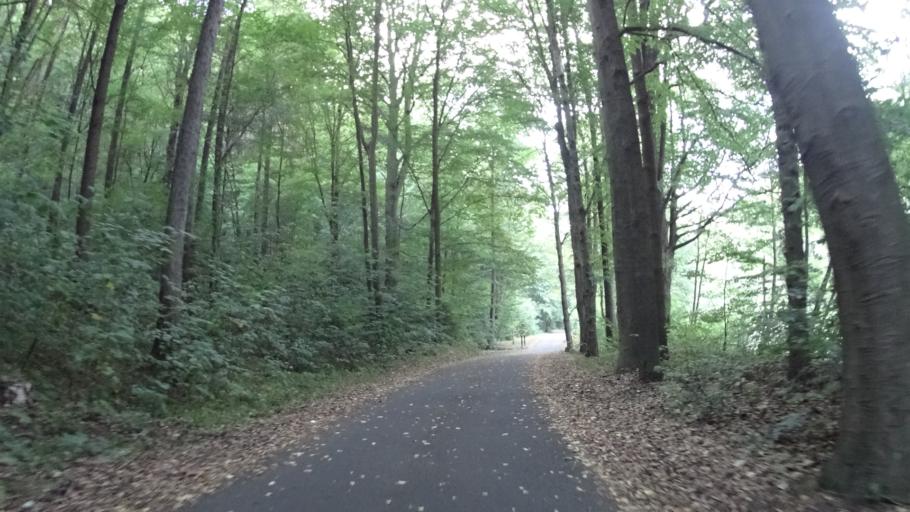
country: DE
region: Saxony
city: Ostritz
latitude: 50.9805
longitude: 14.9181
